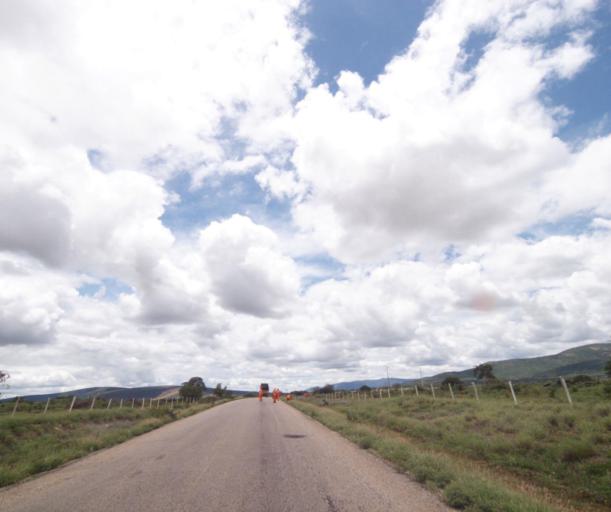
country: BR
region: Bahia
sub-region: Brumado
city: Brumado
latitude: -14.1584
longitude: -41.5238
